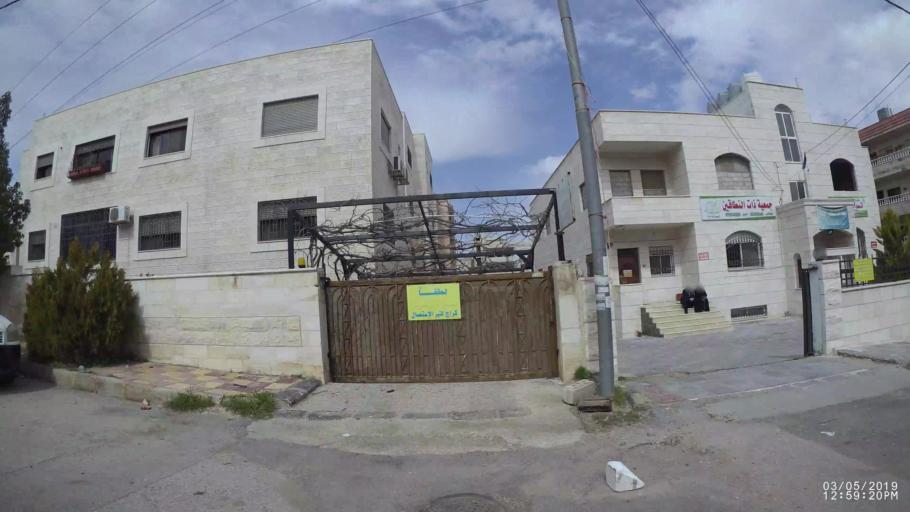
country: JO
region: Amman
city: Amman
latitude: 31.9958
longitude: 35.9371
